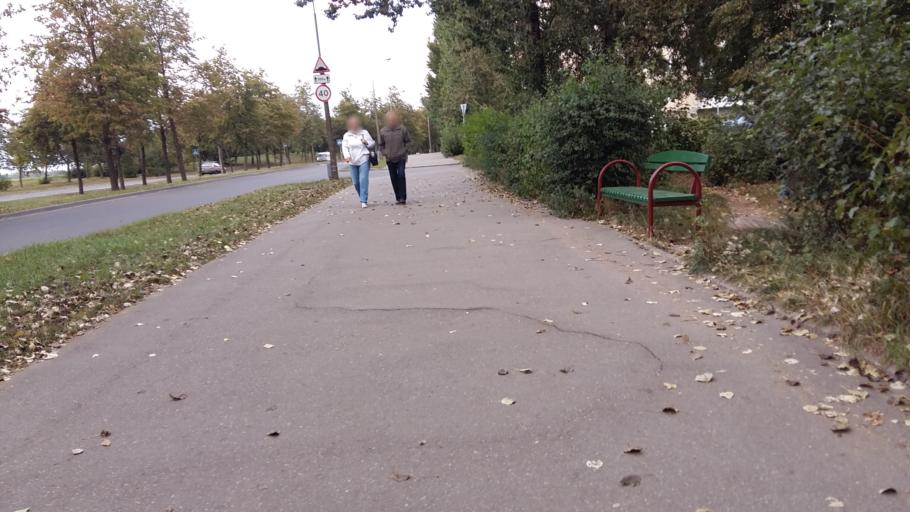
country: BY
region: Grodnenskaya
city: Hrodna
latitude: 53.7011
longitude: 23.7983
